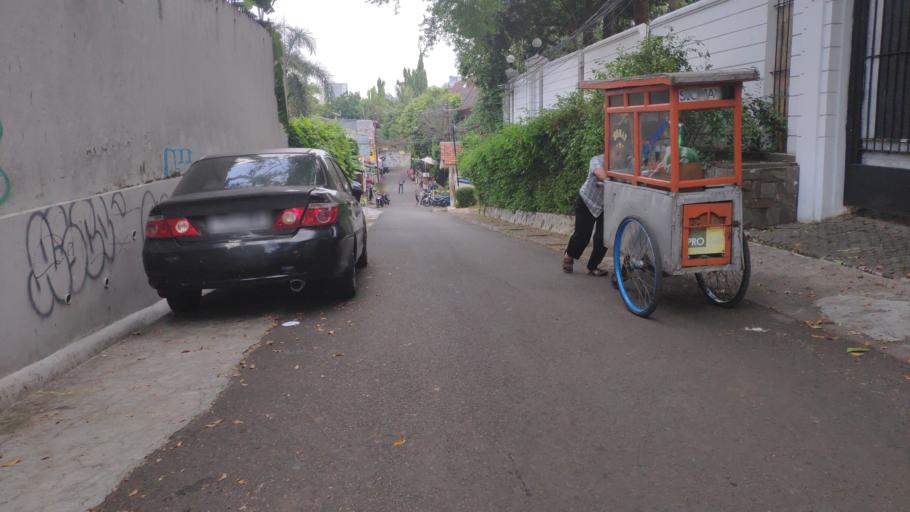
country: ID
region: Jakarta Raya
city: Jakarta
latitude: -6.2716
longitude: 106.8270
